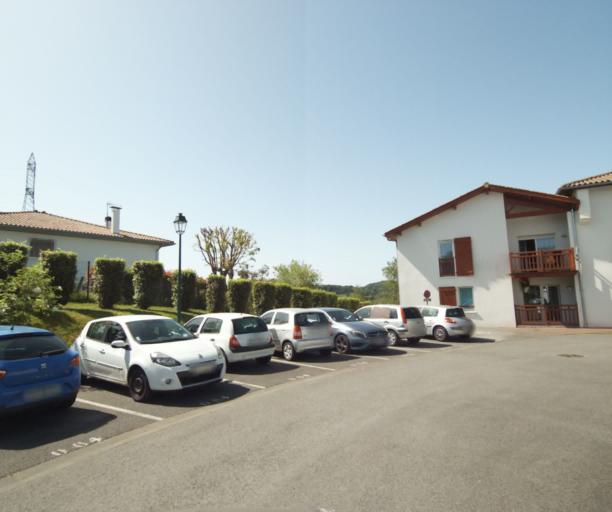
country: FR
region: Aquitaine
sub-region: Departement des Pyrenees-Atlantiques
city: Mouguerre
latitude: 43.4690
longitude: -1.4487
